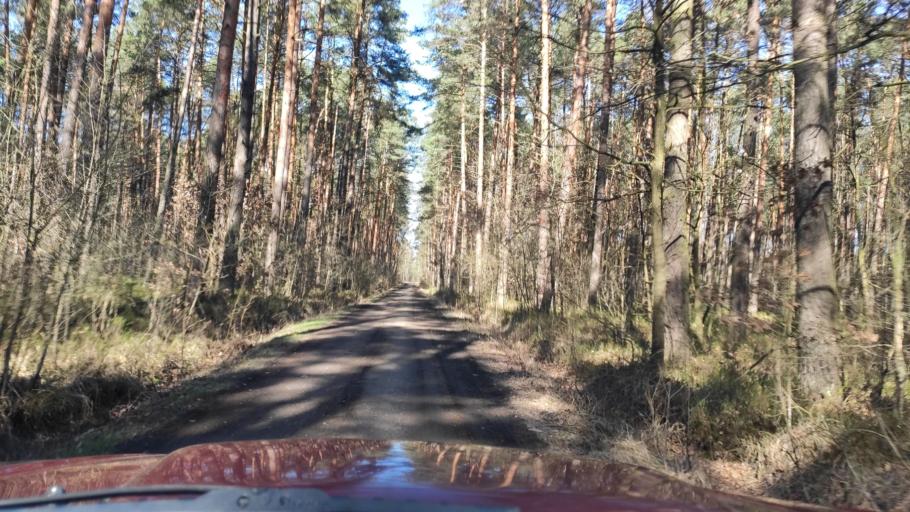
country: PL
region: Masovian Voivodeship
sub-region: Powiat kozienicki
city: Garbatka-Letnisko
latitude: 51.4383
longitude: 21.5438
